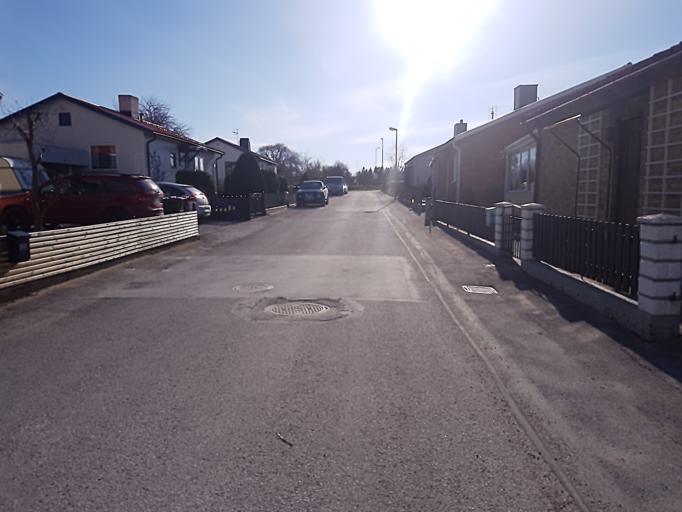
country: SE
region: Gotland
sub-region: Gotland
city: Visby
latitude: 57.6165
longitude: 18.2874
